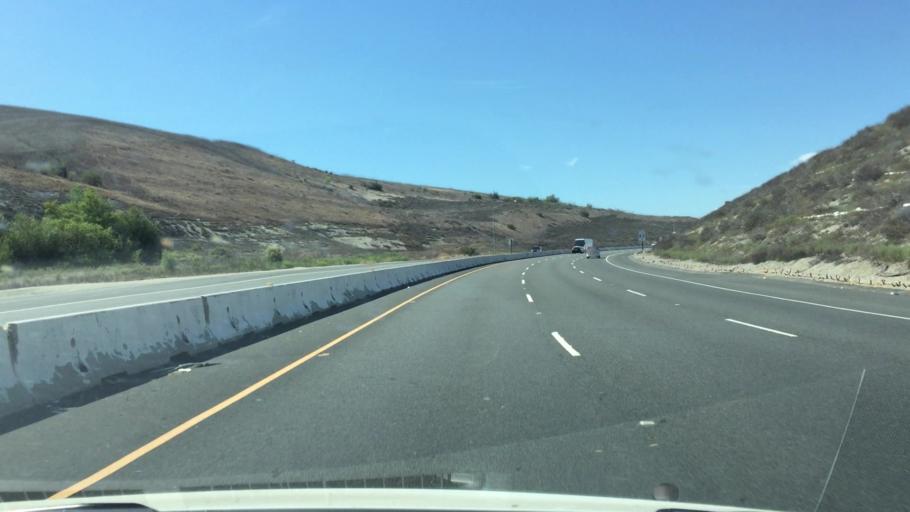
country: US
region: California
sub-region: Orange County
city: North Tustin
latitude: 33.7538
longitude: -117.7318
